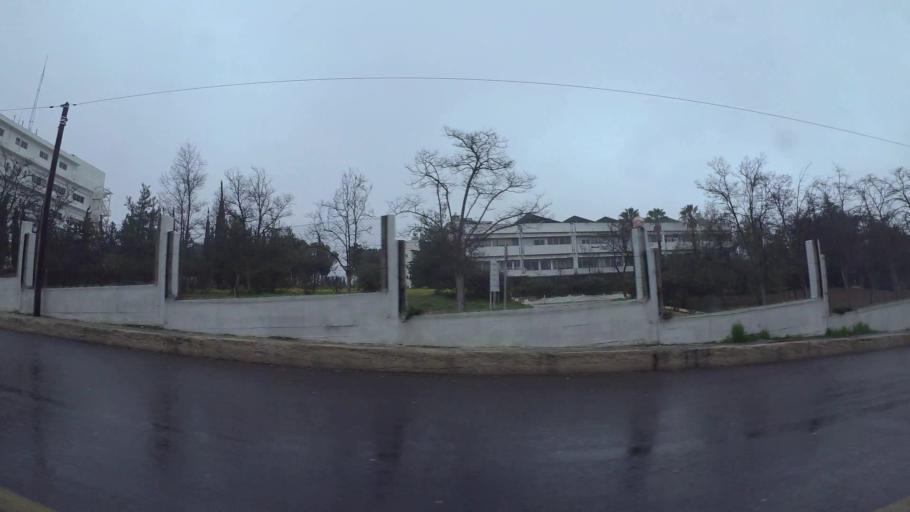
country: JO
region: Amman
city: Al Jubayhah
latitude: 32.0251
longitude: 35.8766
